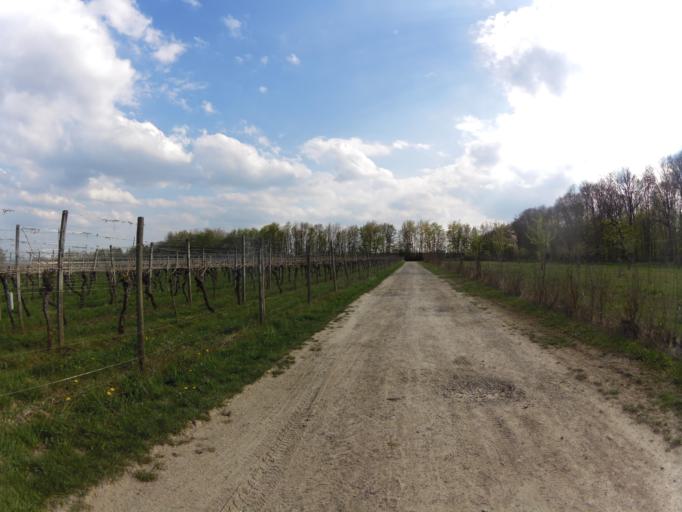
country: DE
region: Bavaria
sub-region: Regierungsbezirk Unterfranken
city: Winterhausen
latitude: 49.6954
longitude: 10.0064
